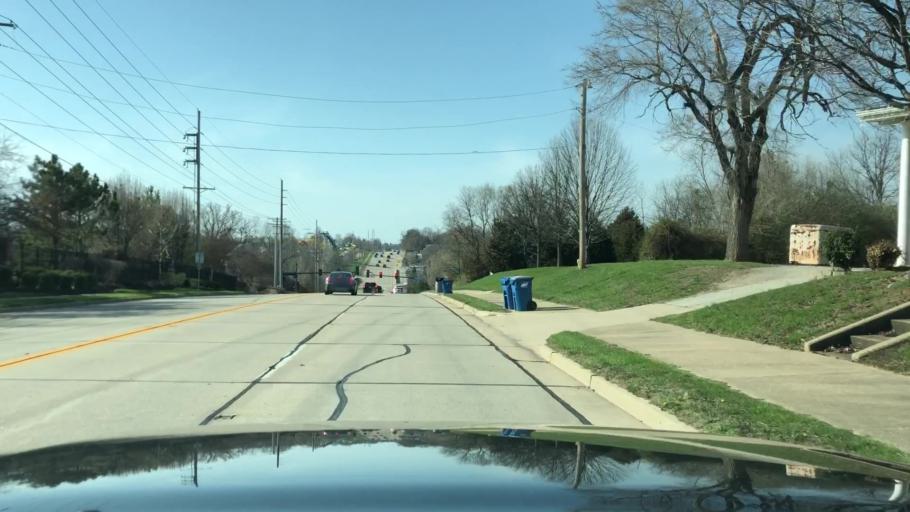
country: US
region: Missouri
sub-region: Saint Charles County
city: Saint Charles
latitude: 38.7636
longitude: -90.5425
